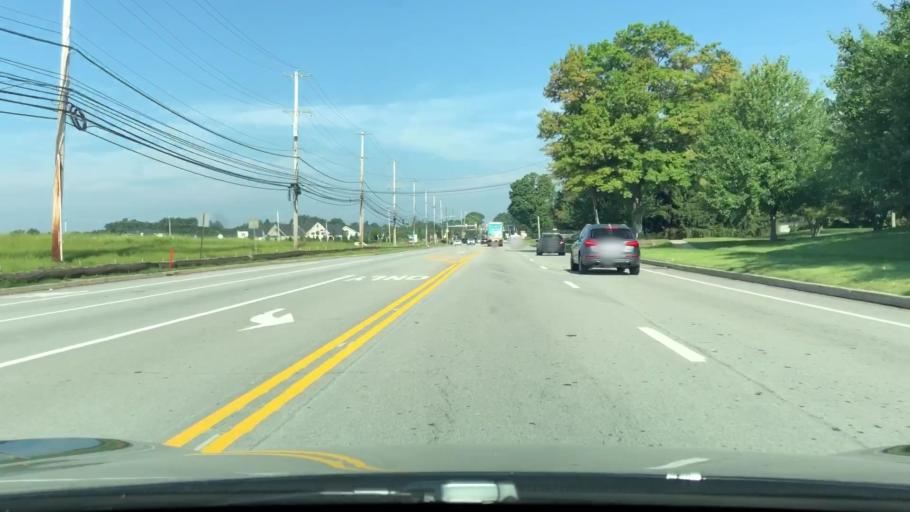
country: US
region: Pennsylvania
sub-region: Montgomery County
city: Horsham
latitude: 40.1592
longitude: -75.1469
